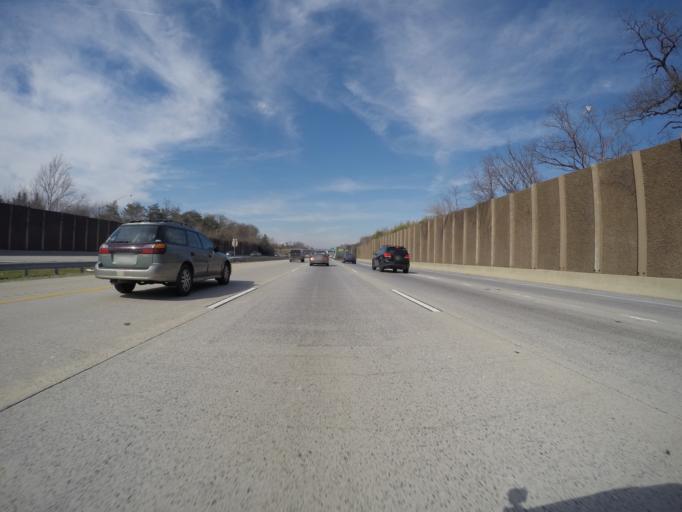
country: US
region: Maryland
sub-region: Anne Arundel County
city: South Gate
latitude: 39.1382
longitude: -76.6439
